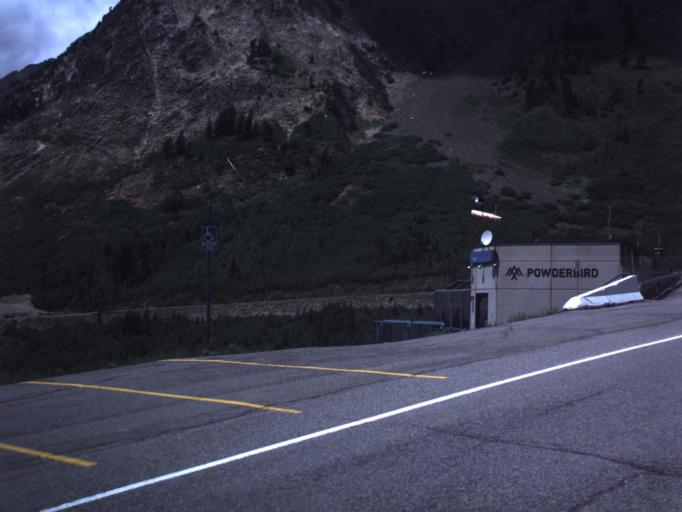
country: US
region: Utah
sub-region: Summit County
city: Snyderville
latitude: 40.5838
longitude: -111.6504
